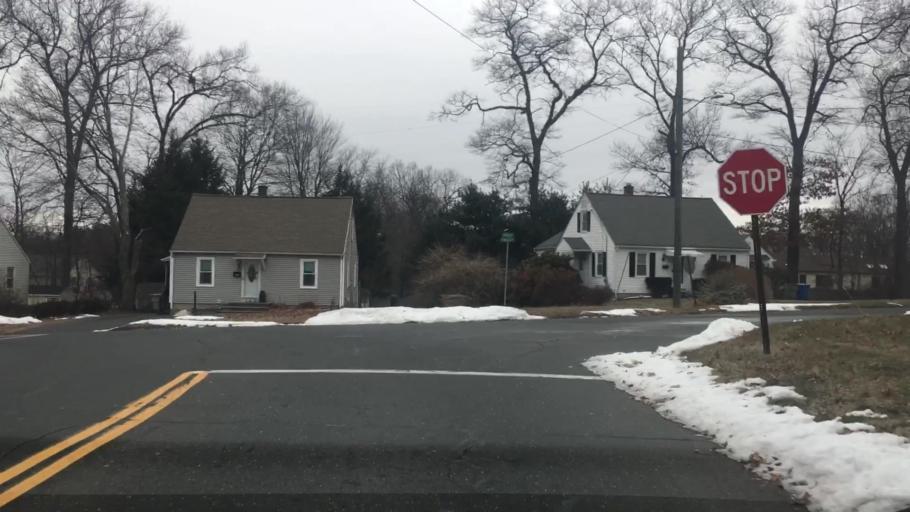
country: US
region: Connecticut
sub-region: Hartford County
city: Bristol
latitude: 41.6819
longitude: -72.9158
